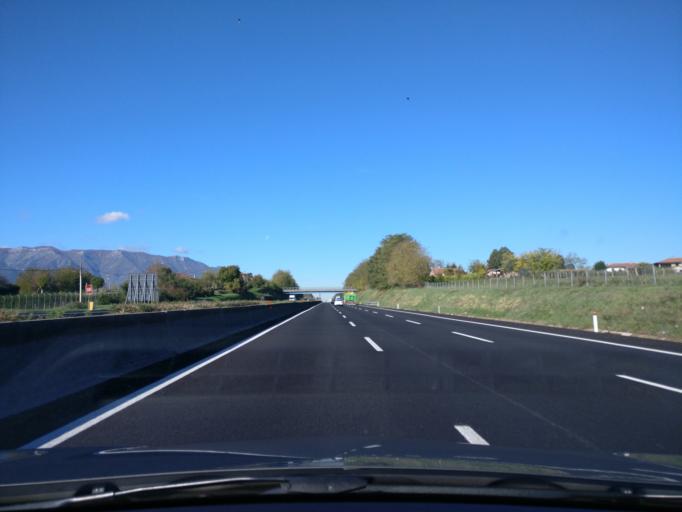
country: IT
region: Latium
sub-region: Provincia di Frosinone
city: Frosinone
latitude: 41.6222
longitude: 13.3050
